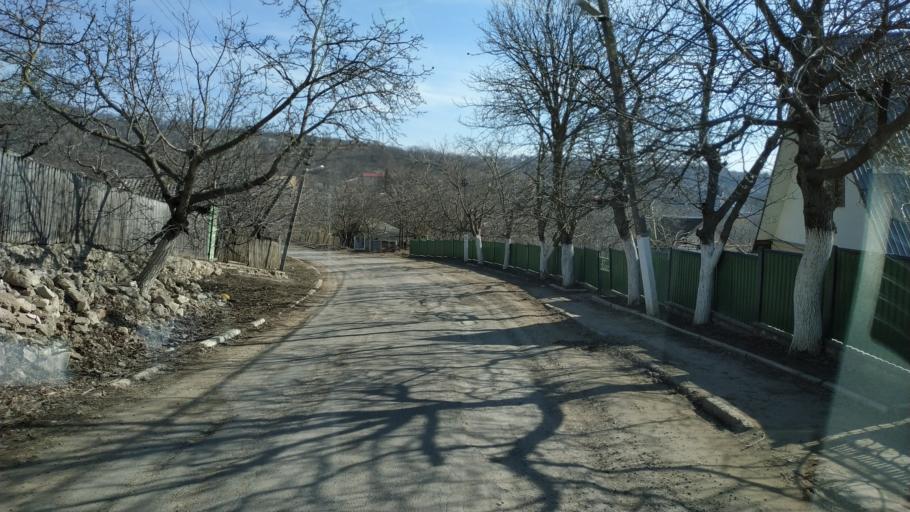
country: MD
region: Nisporeni
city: Nisporeni
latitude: 47.2230
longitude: 28.0400
